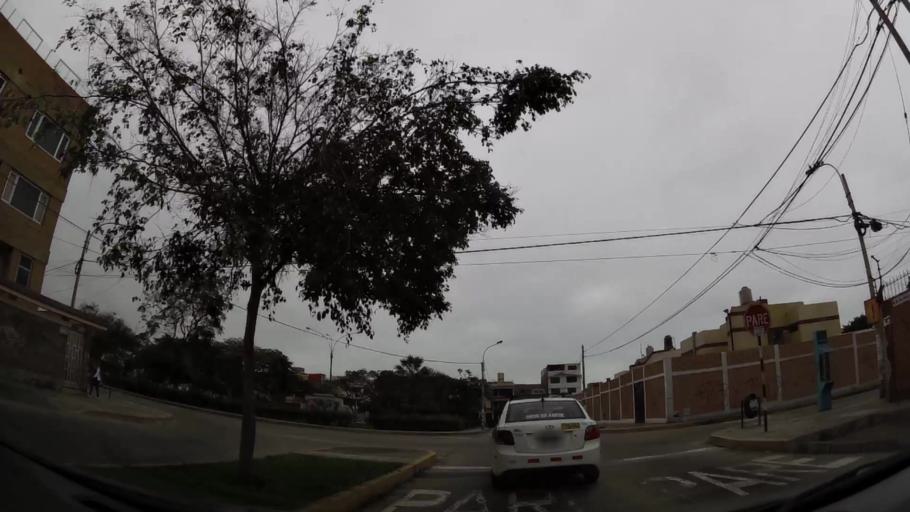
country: PE
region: Callao
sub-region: Callao
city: Callao
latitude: -12.0627
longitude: -77.0751
